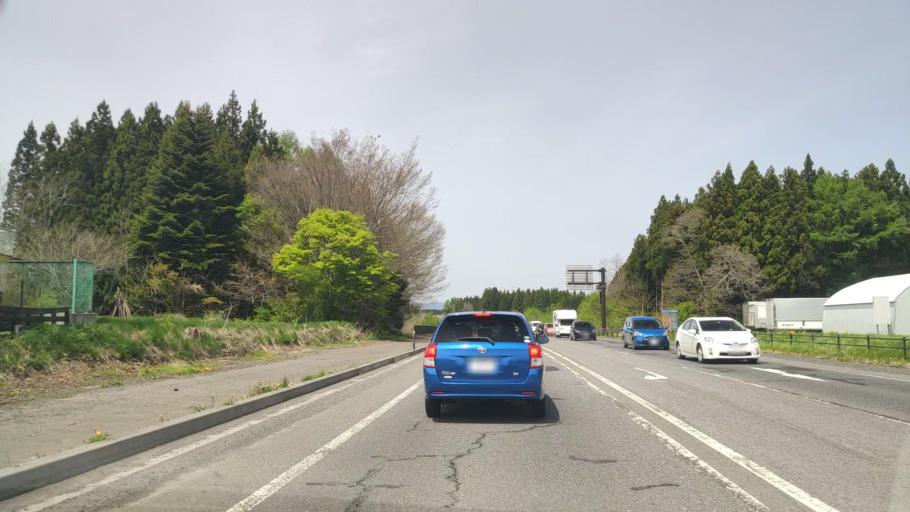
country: JP
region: Aomori
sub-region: Misawa Shi
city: Inuotose
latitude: 40.7085
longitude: 141.1608
